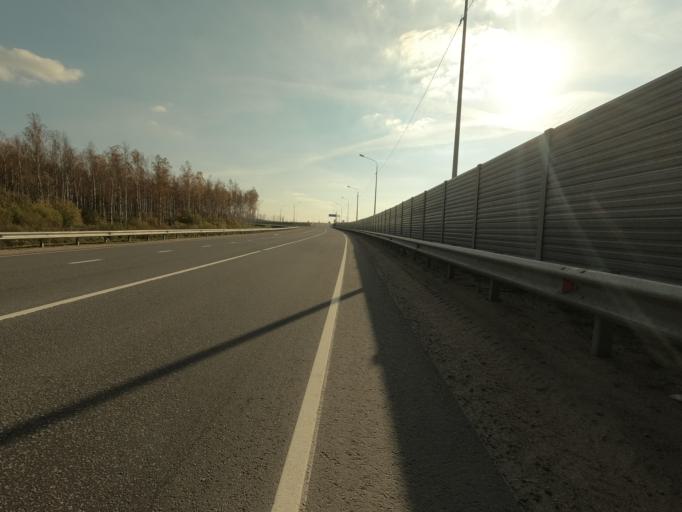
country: RU
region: Leningrad
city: Mga
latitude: 59.7612
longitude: 31.0937
